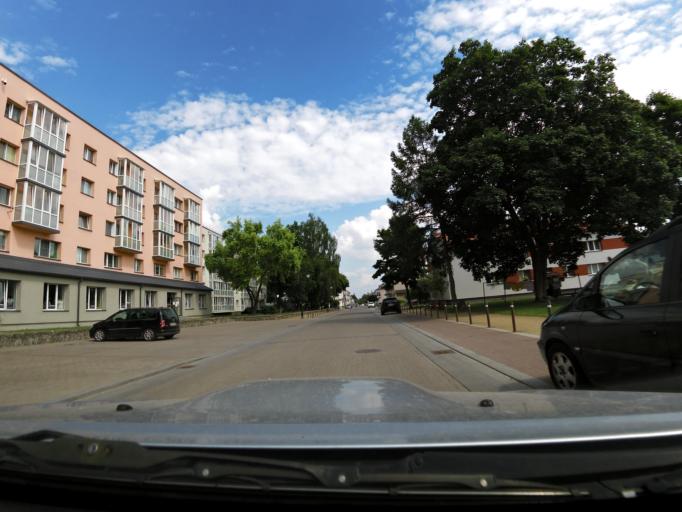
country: LT
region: Taurages apskritis
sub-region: Jurbarkas
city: Jurbarkas
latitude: 55.0759
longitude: 22.7656
